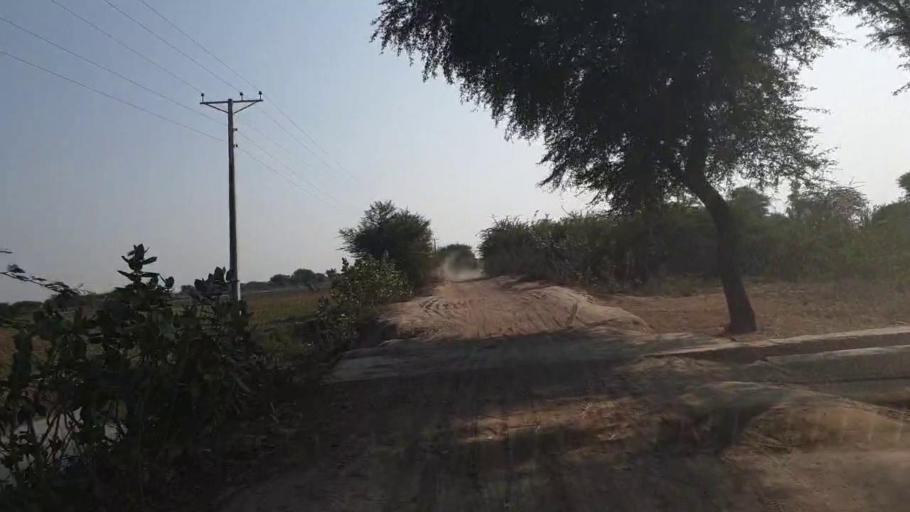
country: PK
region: Sindh
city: Kario
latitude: 24.8914
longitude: 68.6481
